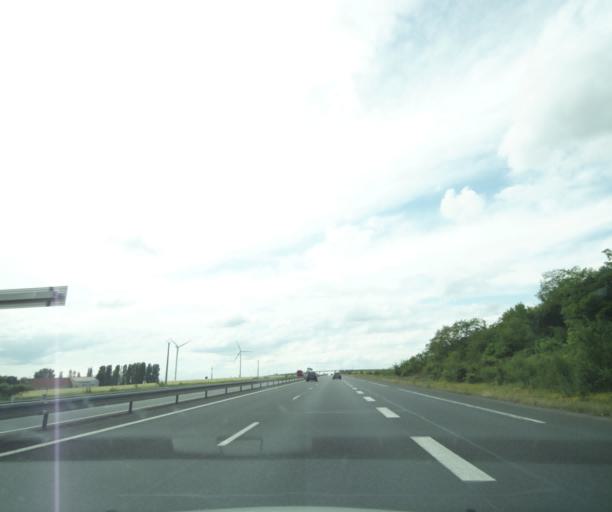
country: FR
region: Centre
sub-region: Departement du Cher
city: Marmagne
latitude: 47.0971
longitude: 2.2365
